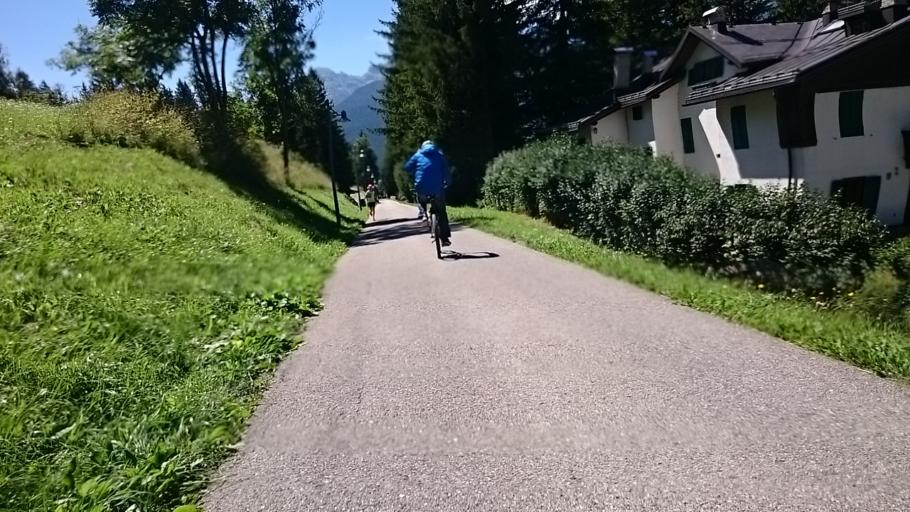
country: IT
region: Veneto
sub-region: Provincia di Belluno
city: Cortina d'Ampezzo
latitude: 46.5317
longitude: 12.1415
